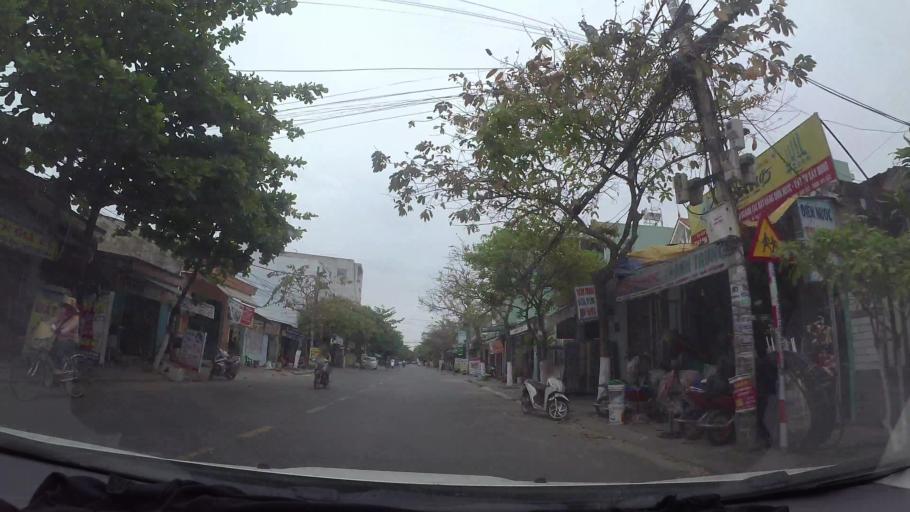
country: VN
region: Da Nang
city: Lien Chieu
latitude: 16.0648
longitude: 108.1507
